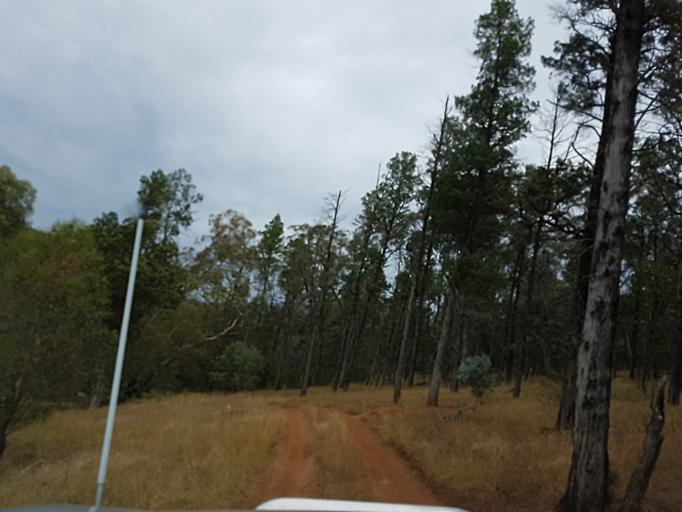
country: AU
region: New South Wales
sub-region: Snowy River
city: Jindabyne
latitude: -36.9342
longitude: 148.4002
